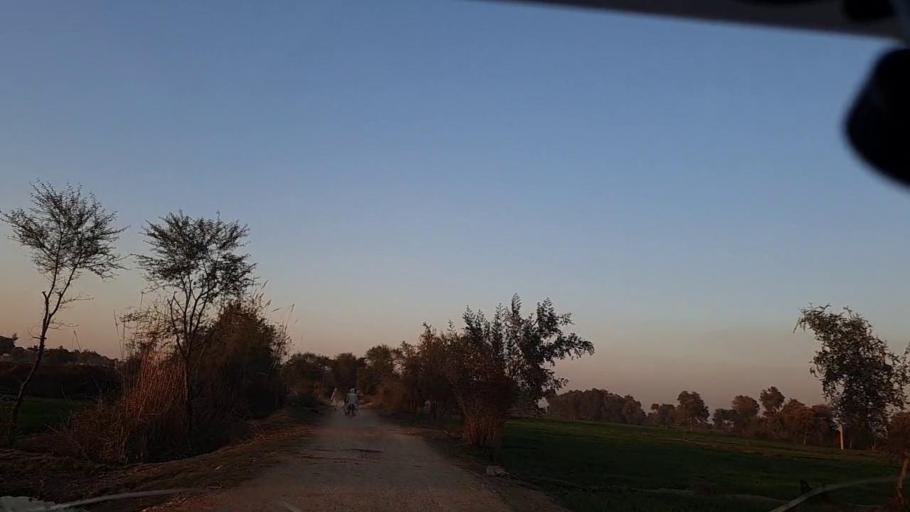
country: PK
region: Sindh
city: Adilpur
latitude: 27.8396
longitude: 69.2983
